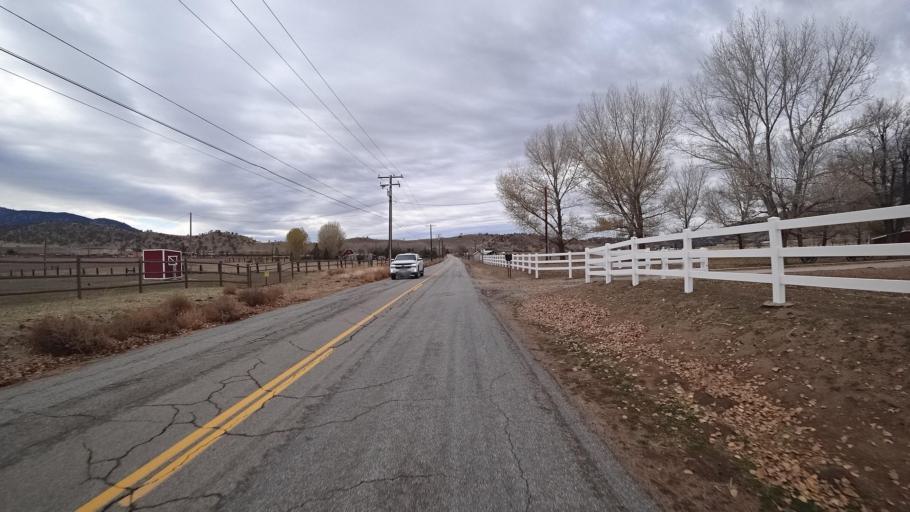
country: US
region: California
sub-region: Kern County
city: Golden Hills
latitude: 35.1167
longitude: -118.5372
